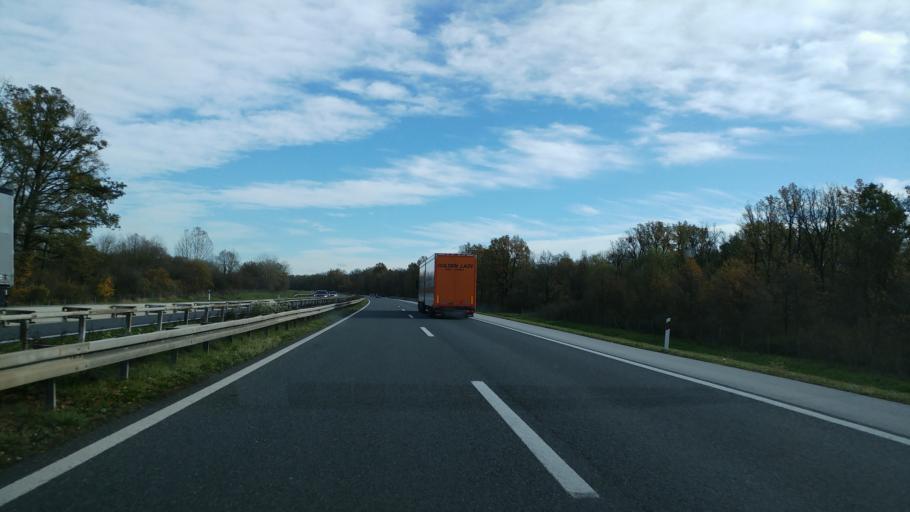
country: HR
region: Sisacko-Moslavacka
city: Kutina
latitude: 45.4512
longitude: 16.7771
